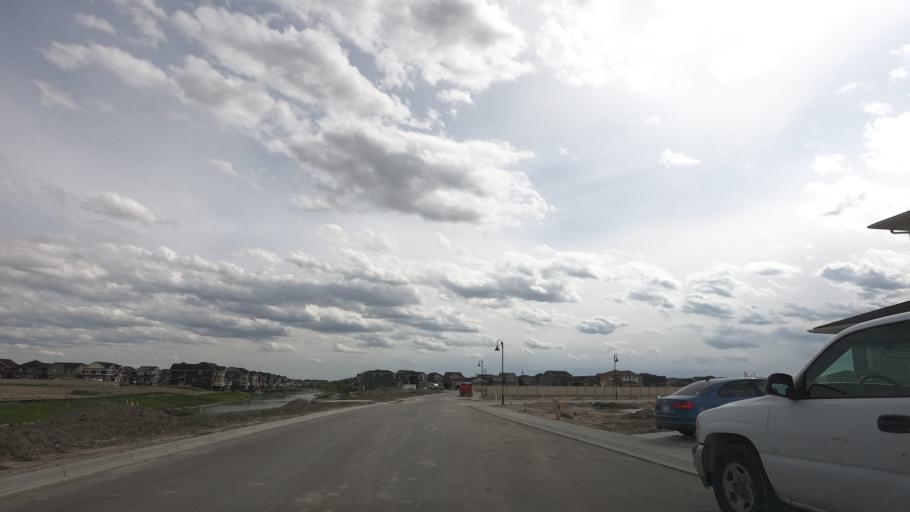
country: CA
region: Alberta
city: Airdrie
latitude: 51.2805
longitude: -114.0407
